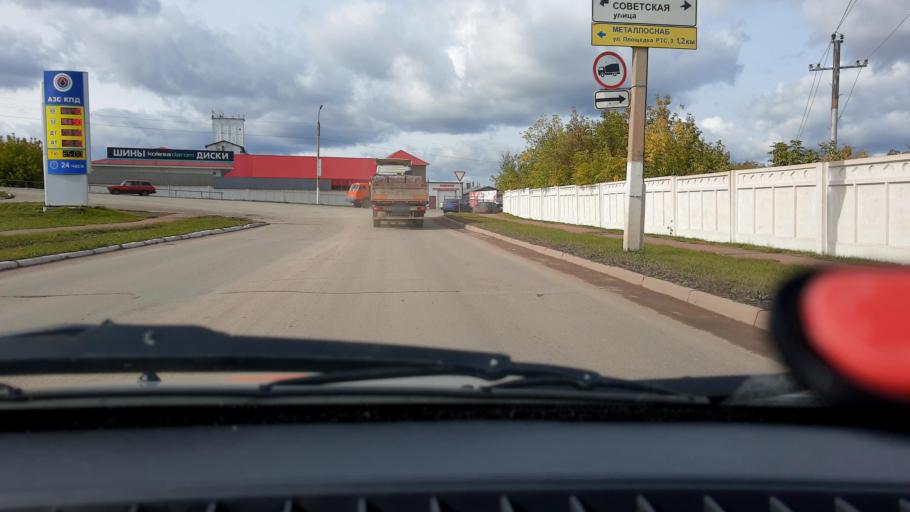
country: RU
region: Bashkortostan
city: Belebey
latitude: 54.0974
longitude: 54.1239
